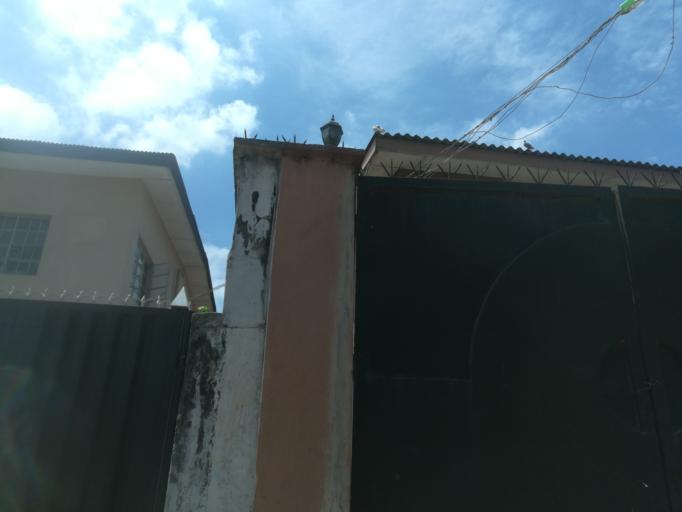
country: NG
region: Lagos
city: Oshodi
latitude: 6.5648
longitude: 3.3326
